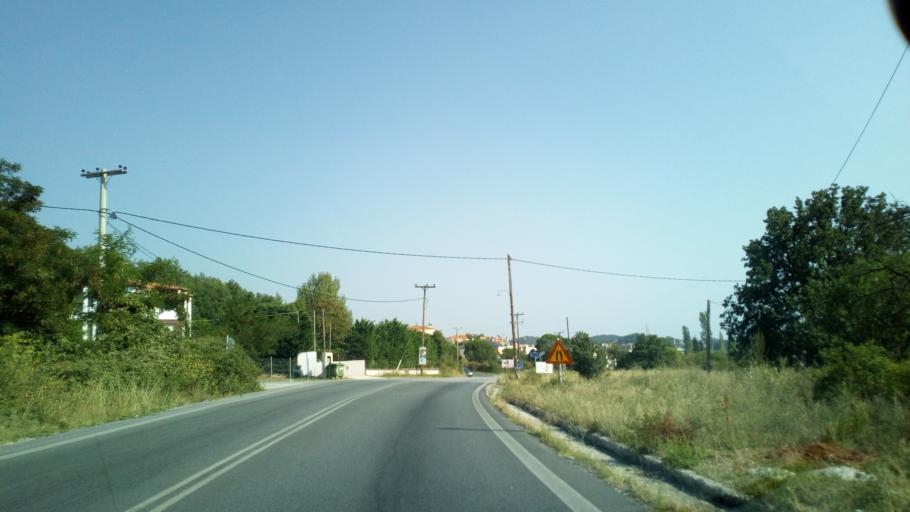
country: GR
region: Central Macedonia
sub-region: Nomos Chalkidikis
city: Polygyros
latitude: 40.3879
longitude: 23.4397
